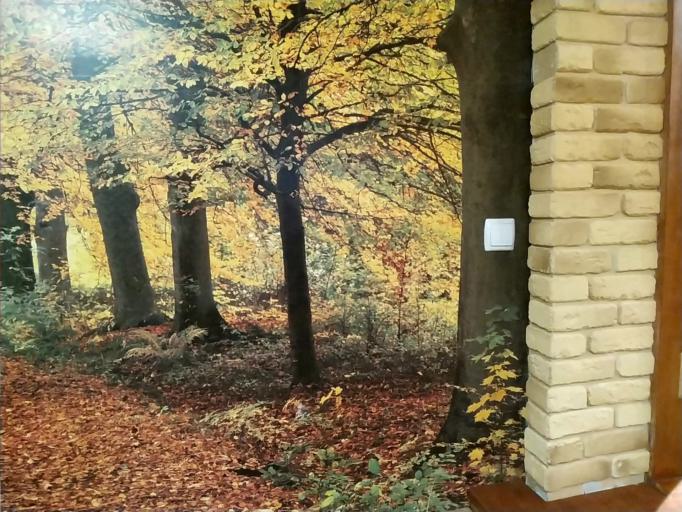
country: RU
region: Smolensk
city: Safonovo
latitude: 55.2005
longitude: 33.2112
